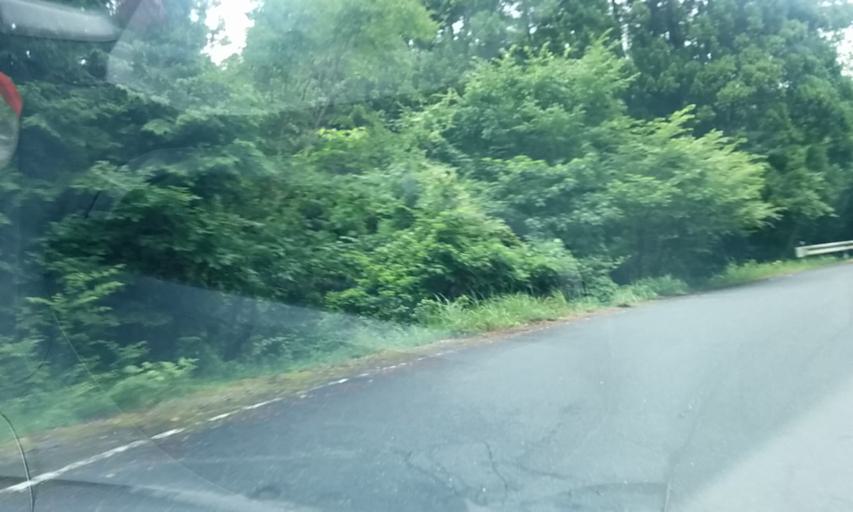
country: JP
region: Kyoto
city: Kameoka
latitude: 35.0509
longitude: 135.4236
